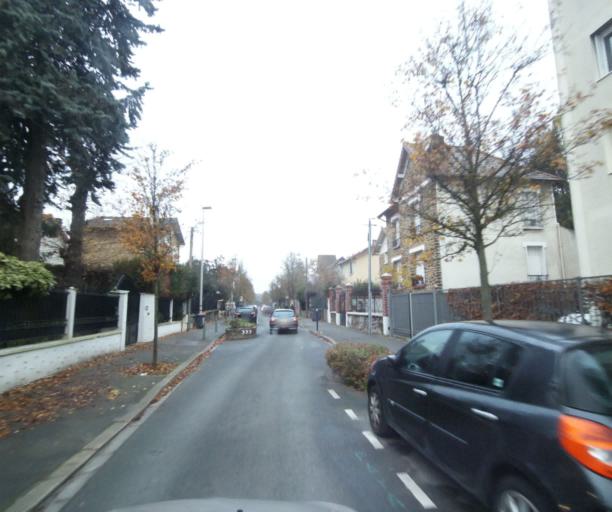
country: FR
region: Ile-de-France
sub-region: Departement de Seine-Saint-Denis
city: Gagny
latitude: 48.8835
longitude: 2.5230
